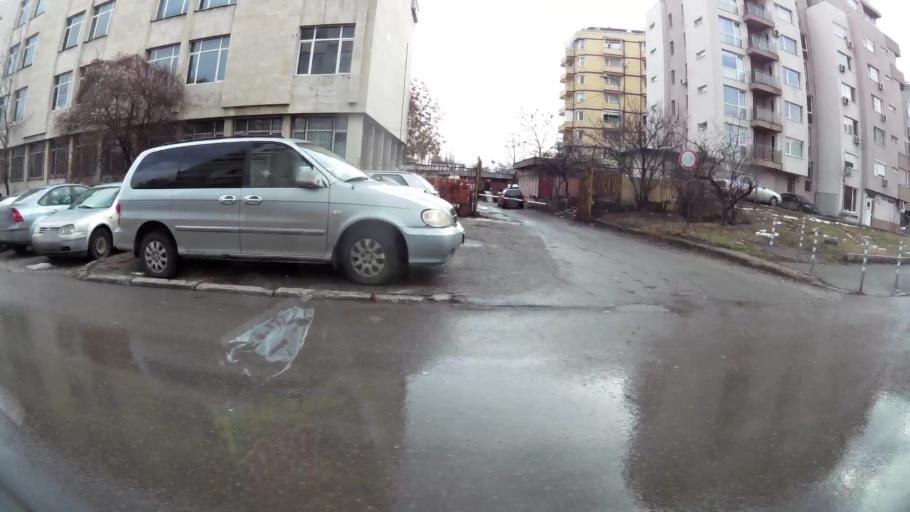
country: BG
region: Sofiya
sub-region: Obshtina Bozhurishte
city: Bozhurishte
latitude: 42.7205
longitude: 23.2520
